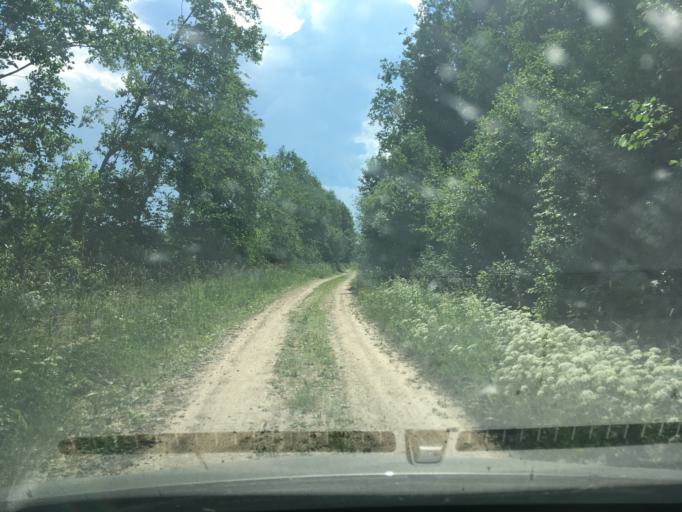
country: EE
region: Raplamaa
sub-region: Maerjamaa vald
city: Marjamaa
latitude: 58.7993
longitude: 24.4603
